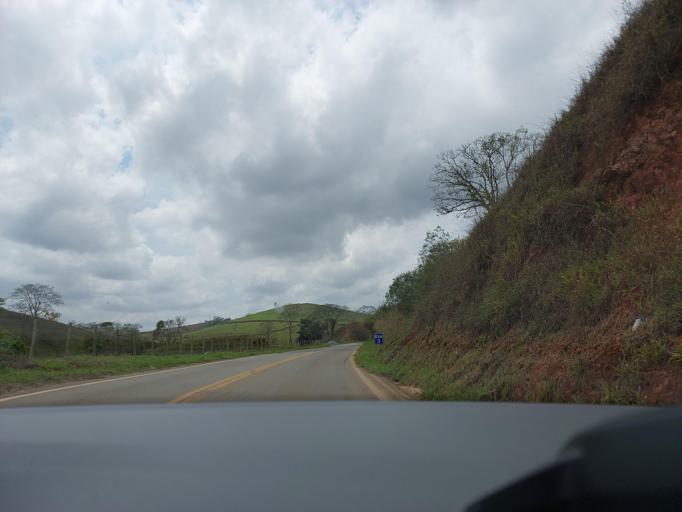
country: BR
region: Minas Gerais
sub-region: Ponte Nova
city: Ponte Nova
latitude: -20.3828
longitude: -42.8866
